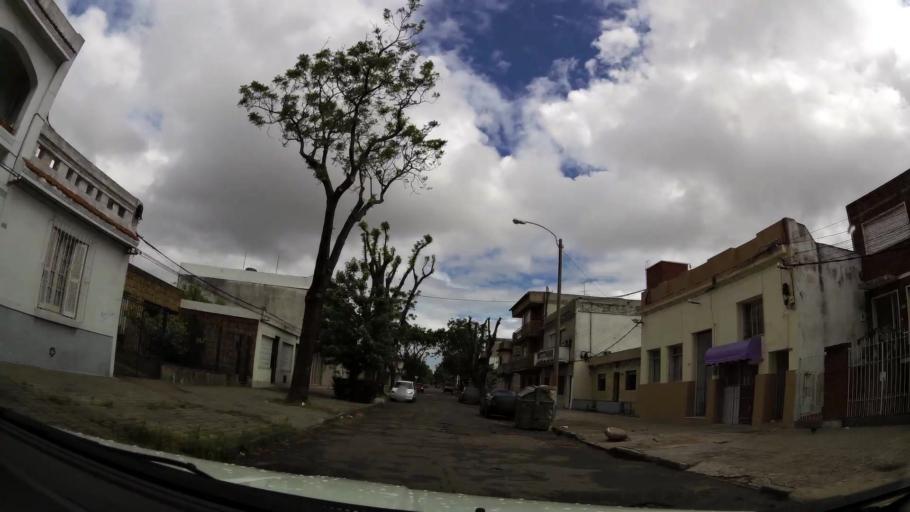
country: UY
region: Montevideo
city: Montevideo
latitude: -34.8723
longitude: -56.1699
